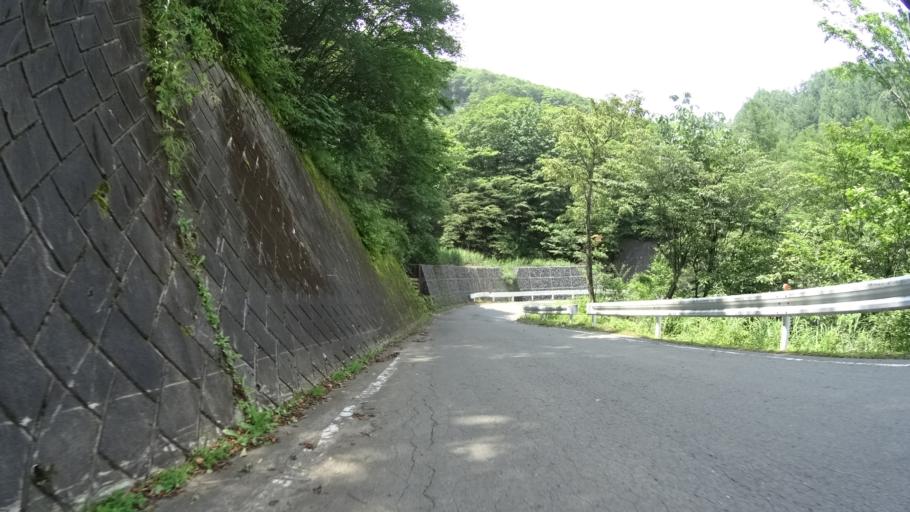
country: JP
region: Nagano
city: Saku
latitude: 36.1025
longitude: 138.6472
